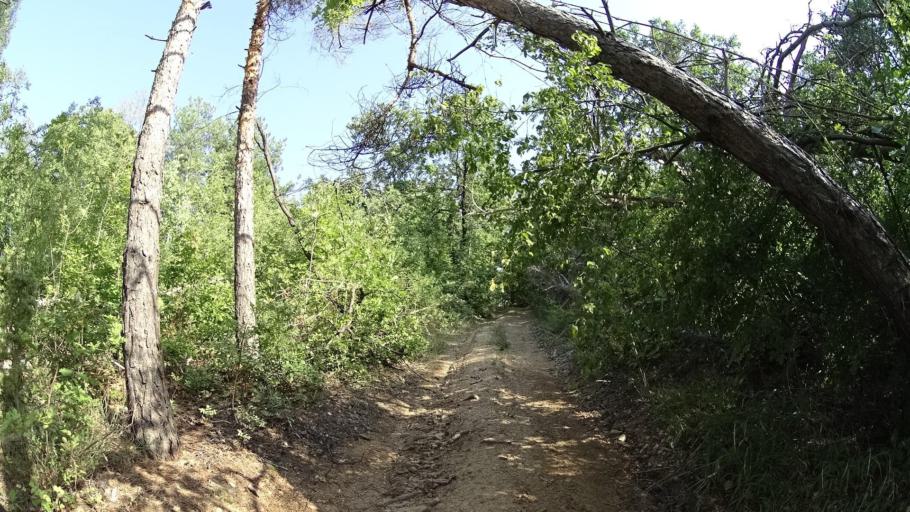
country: BG
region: Plovdiv
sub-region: Obshtina Plovdiv
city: Plovdiv
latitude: 42.0581
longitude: 24.6868
